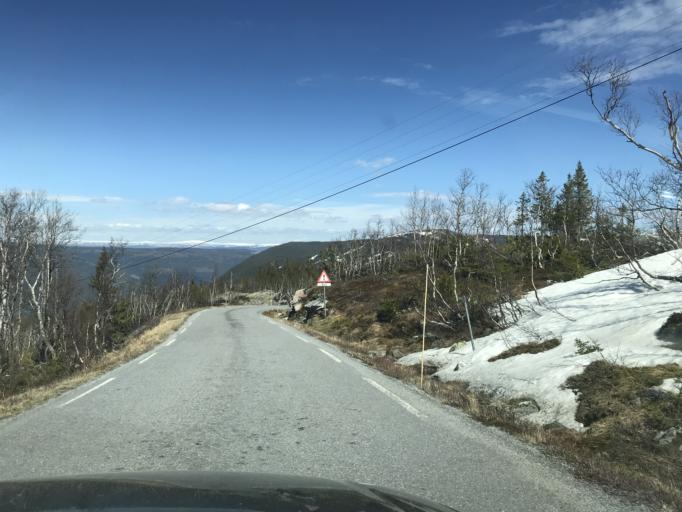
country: NO
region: Telemark
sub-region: Tinn
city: Rjukan
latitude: 59.8662
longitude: 8.6875
